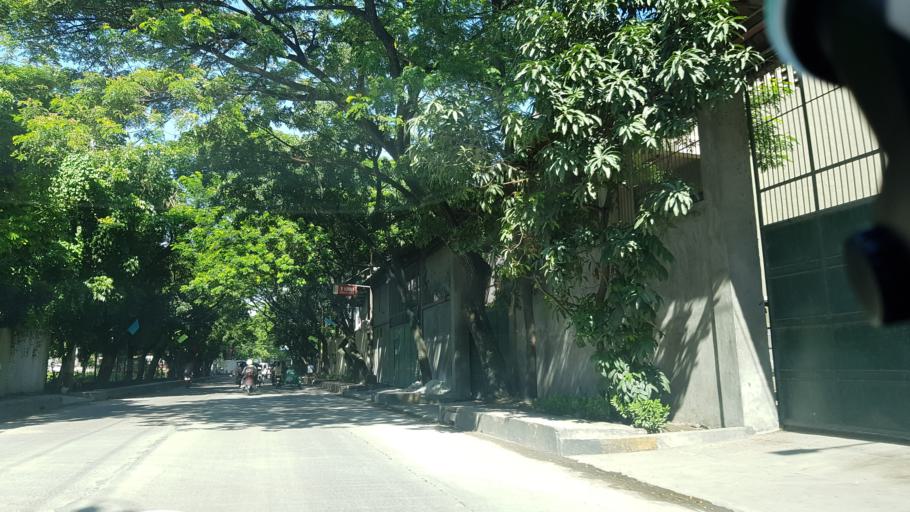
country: PH
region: Calabarzon
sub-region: Province of Rizal
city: Cainta
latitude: 14.5710
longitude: 121.0929
